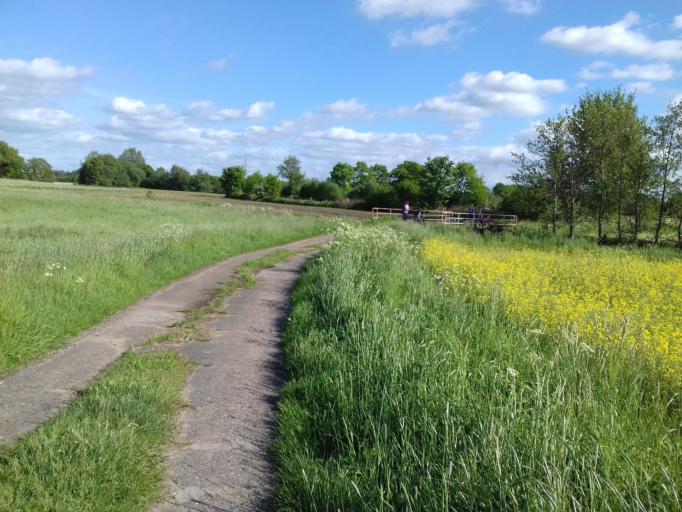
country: DE
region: Schleswig-Holstein
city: Gross Kummerfeld
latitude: 54.0688
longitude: 10.1044
